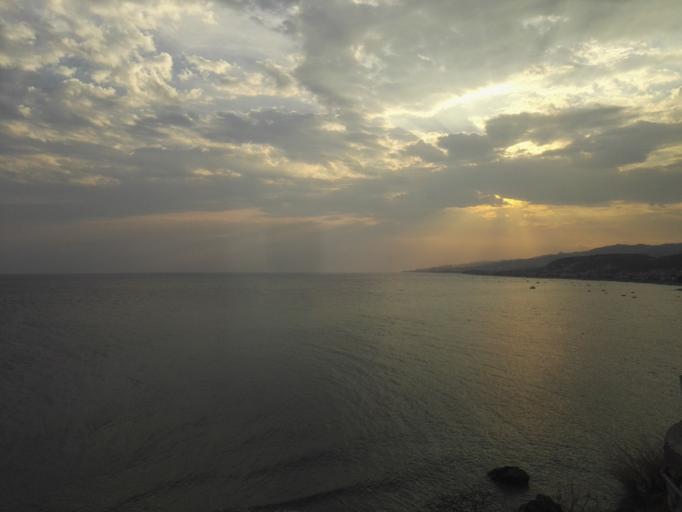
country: IT
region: Calabria
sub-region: Provincia di Reggio Calabria
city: Bova Marina
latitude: 37.9259
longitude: 15.9359
